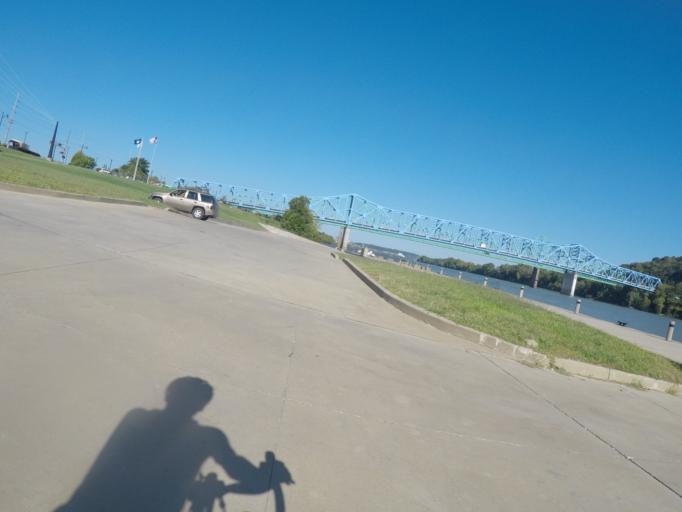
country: US
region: Kentucky
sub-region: Boyd County
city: Ashland
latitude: 38.4814
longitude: -82.6377
